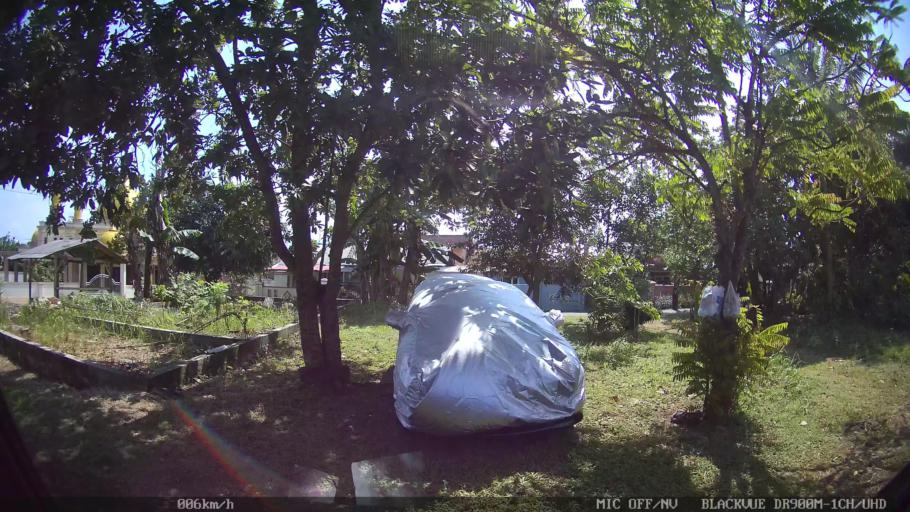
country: ID
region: Lampung
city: Kedaton
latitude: -5.3671
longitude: 105.2540
